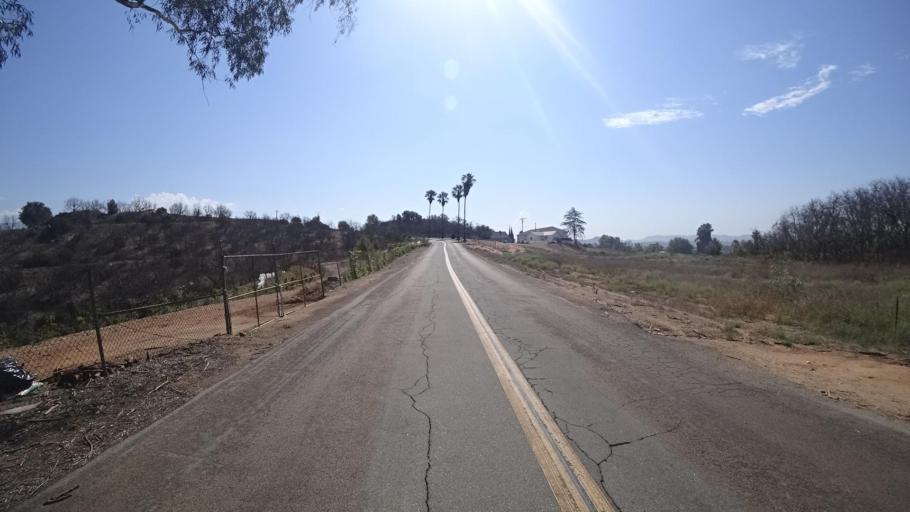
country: US
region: California
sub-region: San Diego County
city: Valley Center
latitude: 33.2950
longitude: -117.0412
